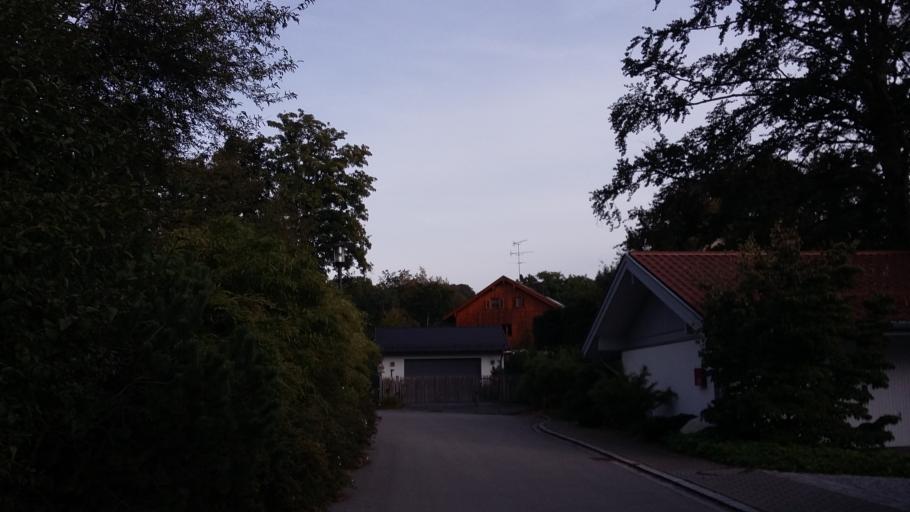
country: DE
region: Bavaria
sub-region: Upper Bavaria
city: Bernried
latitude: 47.8718
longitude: 11.3332
